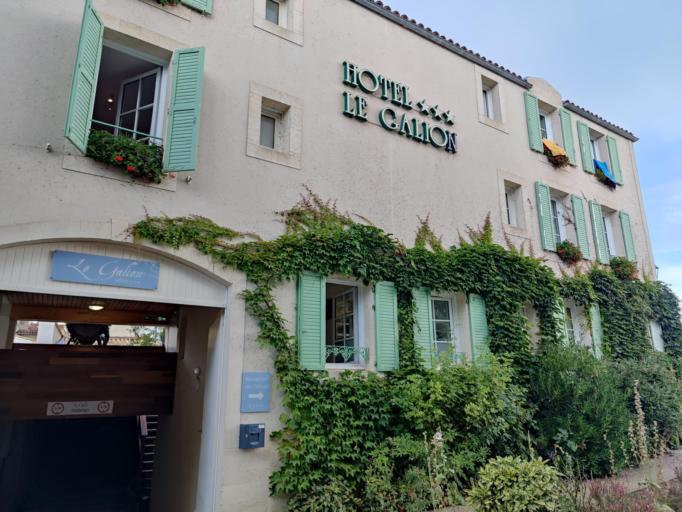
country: FR
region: Poitou-Charentes
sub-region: Departement de la Charente-Maritime
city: Saint-Martin-de-Re
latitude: 46.2060
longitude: -1.3653
